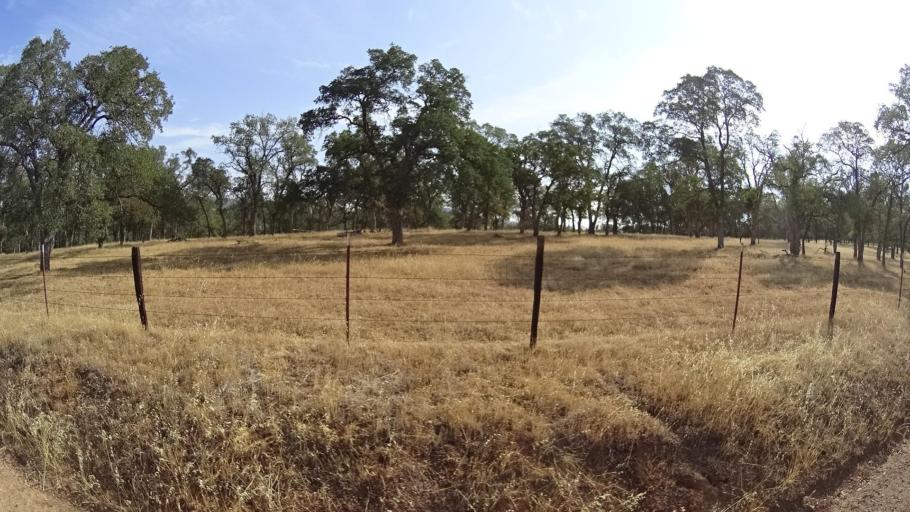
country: US
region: California
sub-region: Tuolumne County
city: Tuolumne City
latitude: 37.7030
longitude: -120.2924
